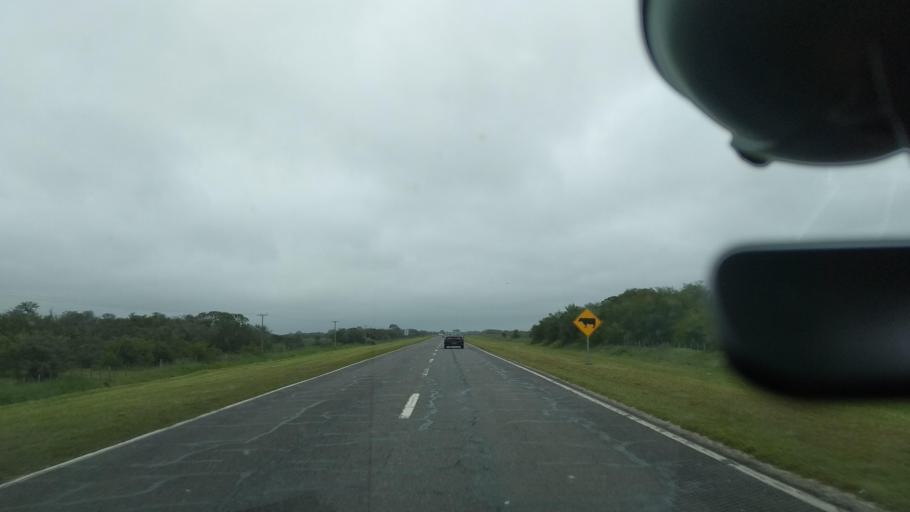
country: AR
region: Buenos Aires
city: Veronica
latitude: -35.6438
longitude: -57.3147
